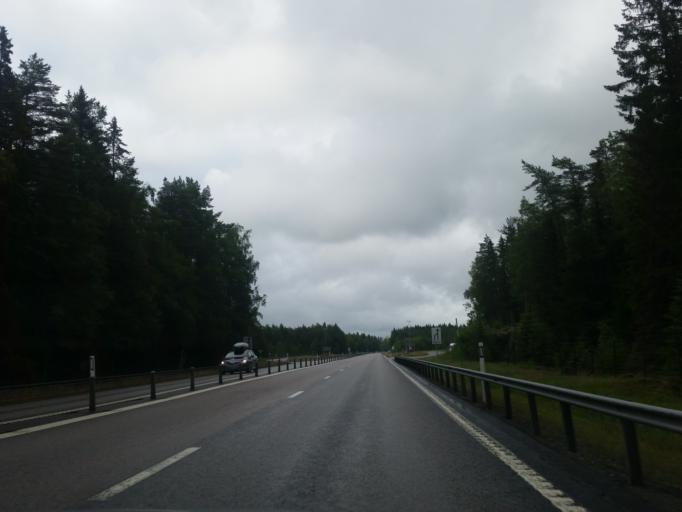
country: SE
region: Vaesterbotten
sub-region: Umea Kommun
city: Saevar
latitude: 63.9102
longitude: 20.5885
